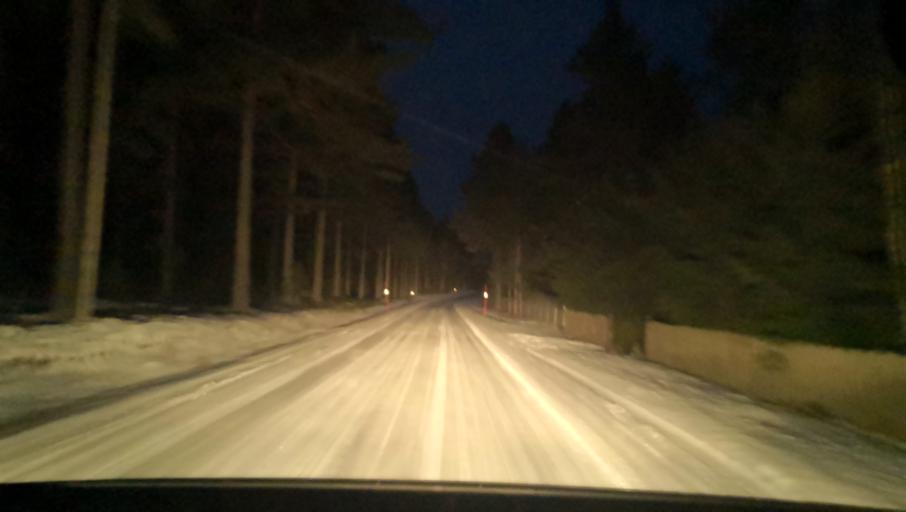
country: SE
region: Uppsala
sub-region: Heby Kommun
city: Tarnsjo
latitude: 60.2828
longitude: 16.8047
